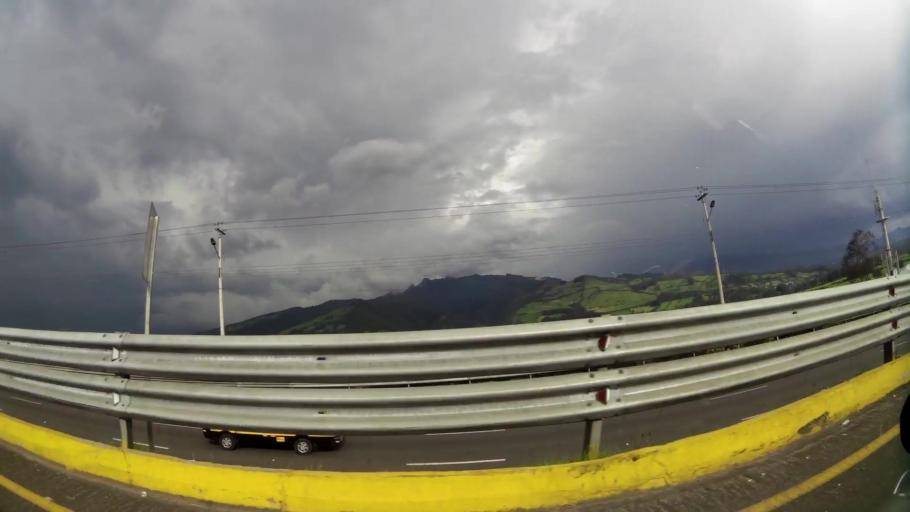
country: EC
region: Pichincha
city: Sangolqui
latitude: -0.4009
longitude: -78.5420
